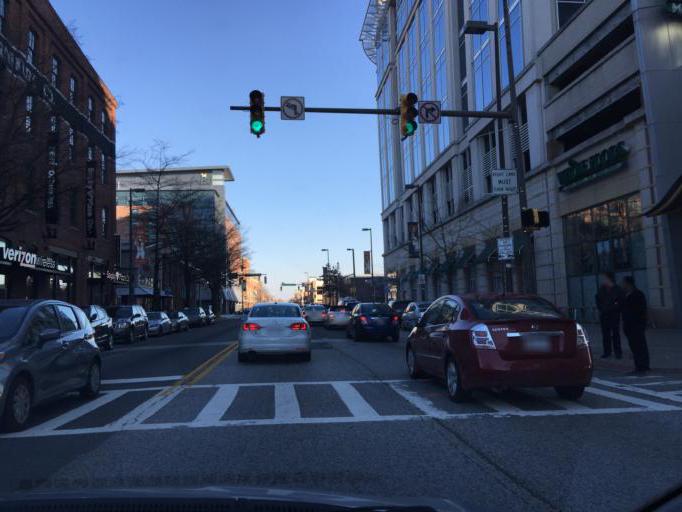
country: US
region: Maryland
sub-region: City of Baltimore
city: Baltimore
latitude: 39.2843
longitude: -76.6003
